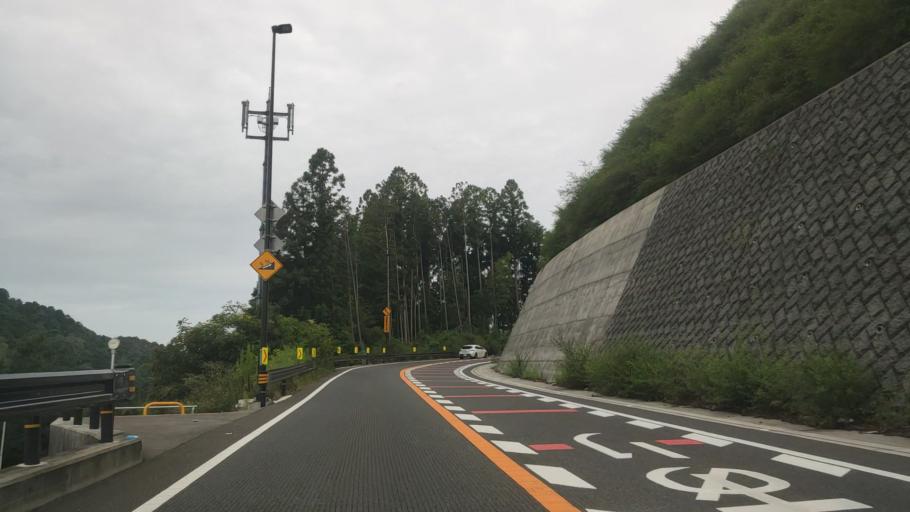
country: JP
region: Wakayama
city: Hashimoto
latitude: 34.3945
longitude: 135.5959
